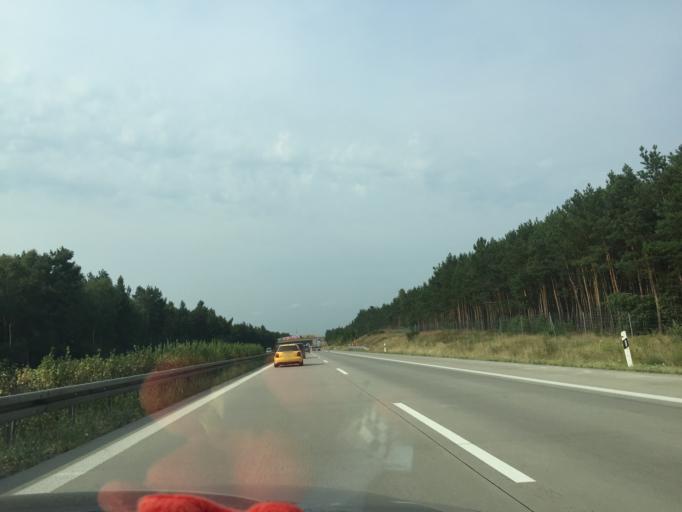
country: DE
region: Brandenburg
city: Teupitz
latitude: 52.1039
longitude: 13.6471
